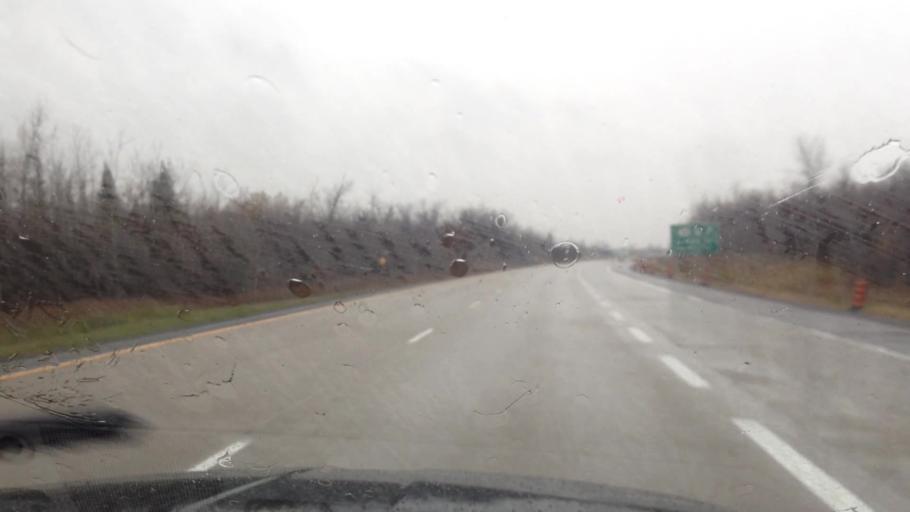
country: CA
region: Ontario
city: Hawkesbury
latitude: 45.4618
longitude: -74.6883
